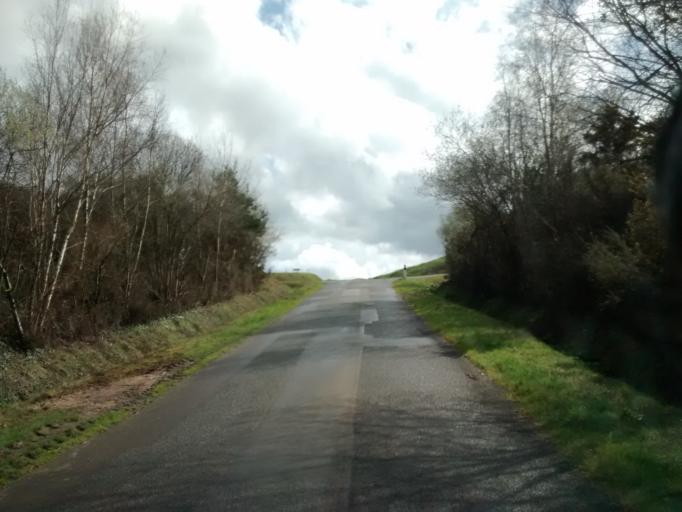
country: FR
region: Brittany
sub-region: Departement d'Ille-et-Vilaine
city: Saint-Thurial
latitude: 48.0390
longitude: -1.9585
